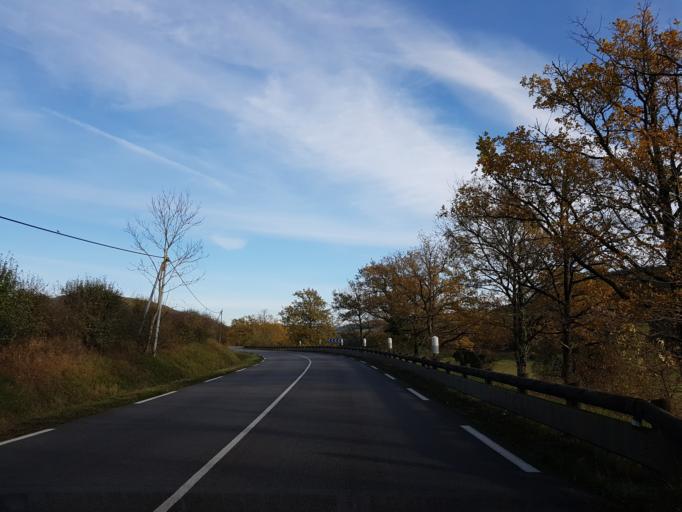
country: FR
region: Bourgogne
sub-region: Departement de la Cote-d'Or
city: Pouilly-en-Auxois
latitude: 47.3088
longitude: 4.6162
